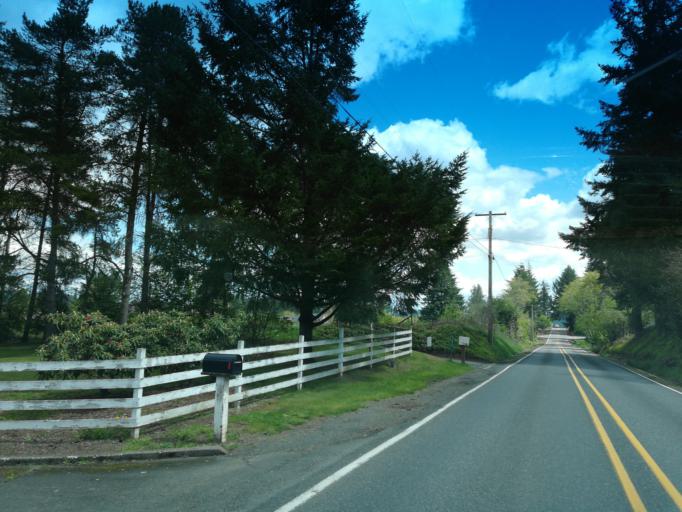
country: US
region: Oregon
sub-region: Clackamas County
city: Damascus
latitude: 45.4397
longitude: -122.4374
